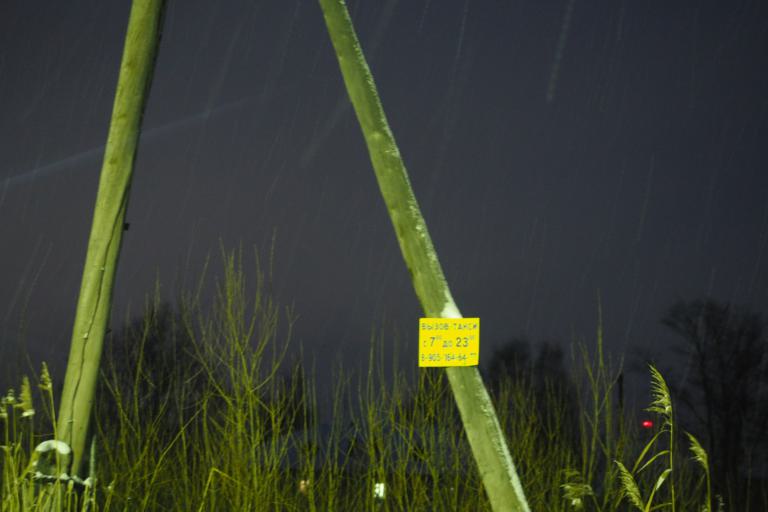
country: RU
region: Tverskaya
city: Krasnyy Kholm
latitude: 58.0489
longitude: 37.1059
